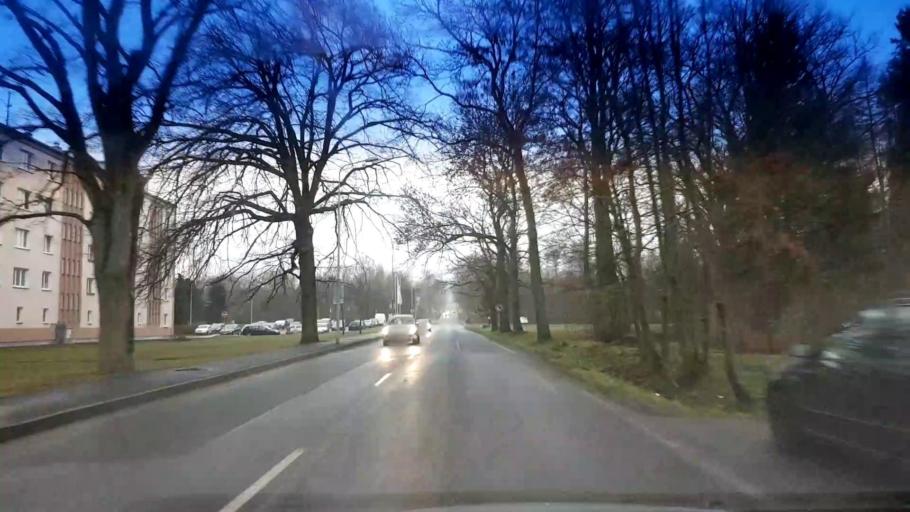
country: CZ
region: Karlovarsky
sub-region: Okres Cheb
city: Cheb
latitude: 50.0679
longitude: 12.3620
